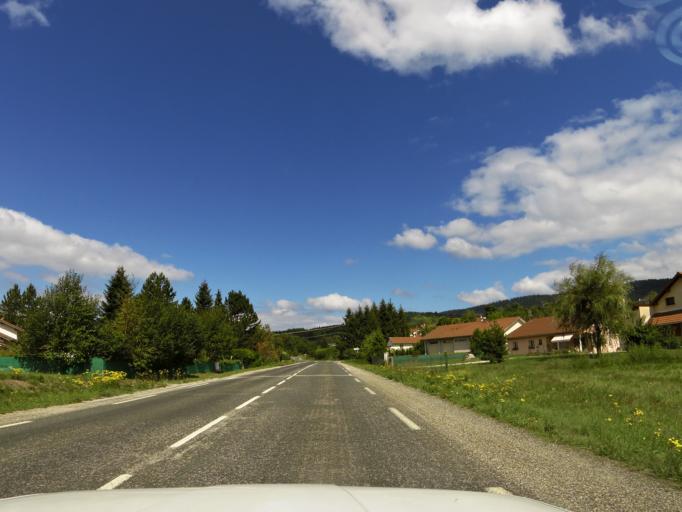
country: FR
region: Rhone-Alpes
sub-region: Departement de l'Ain
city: Hauteville-Lompnes
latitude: 45.9834
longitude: 5.5980
